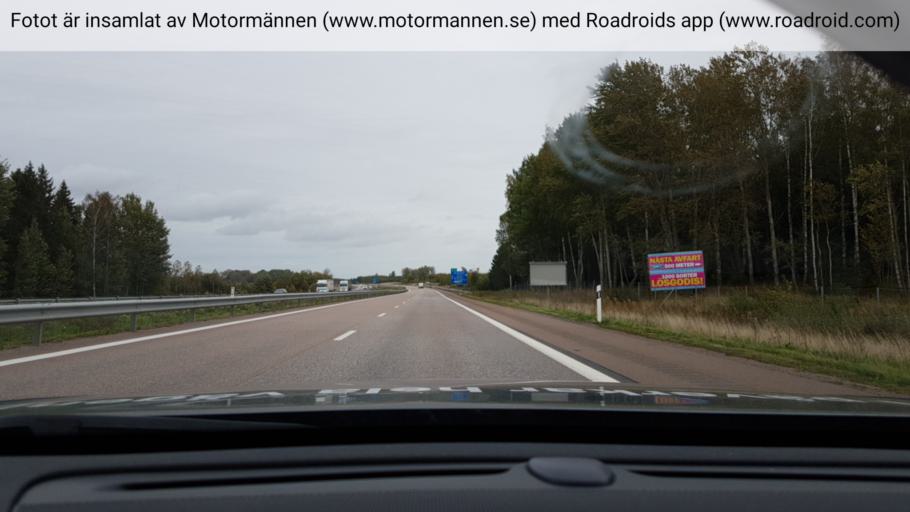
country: SE
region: OEstergoetland
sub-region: Mjolby Kommun
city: Mjolby
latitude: 58.3228
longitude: 15.0764
